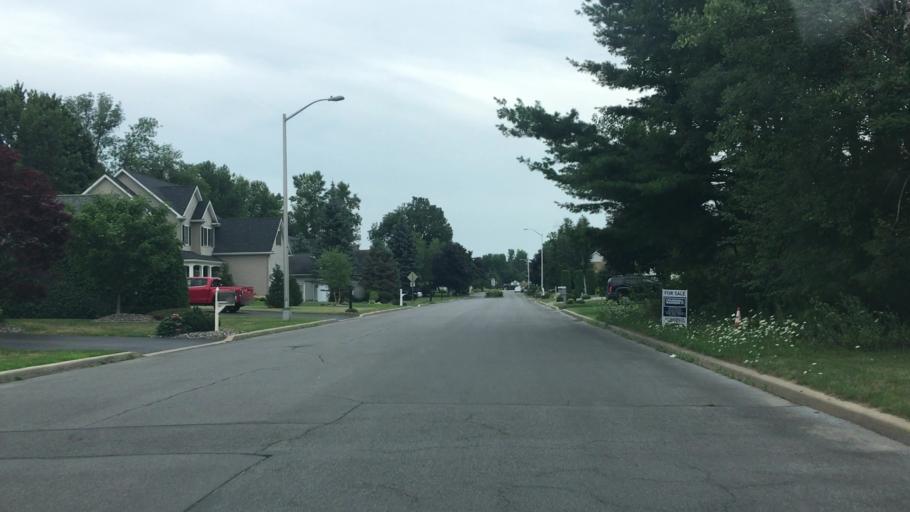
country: US
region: New York
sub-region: Clinton County
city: Plattsburgh West
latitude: 44.6915
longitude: -73.4827
